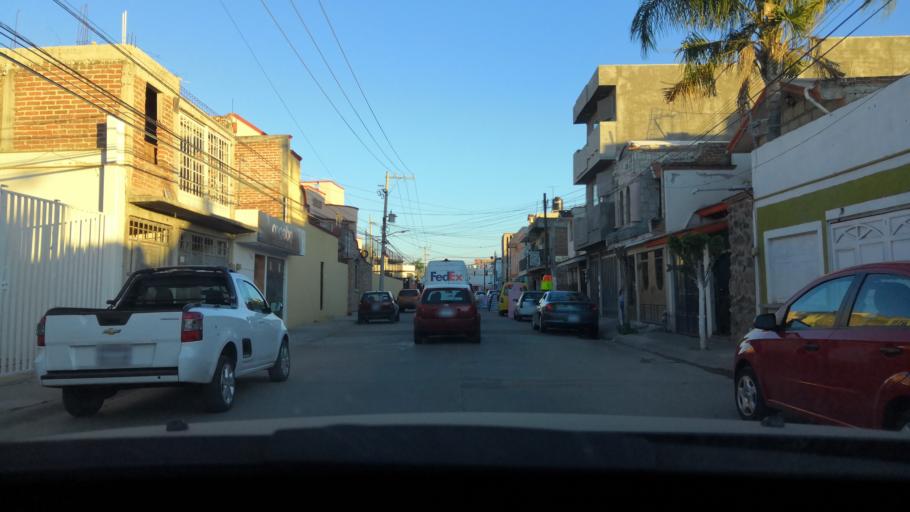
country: MX
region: Guanajuato
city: Leon
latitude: 21.1656
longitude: -101.6598
